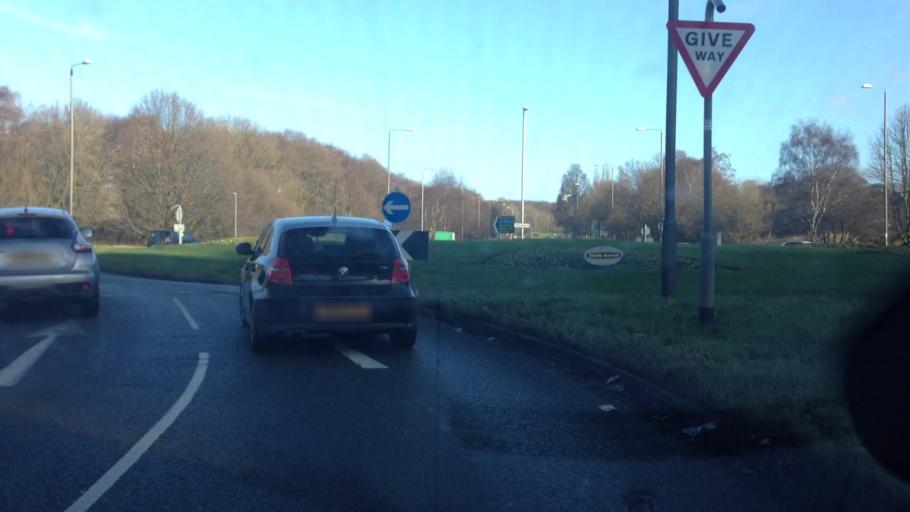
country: GB
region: England
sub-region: City and Borough of Leeds
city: Chapel Allerton
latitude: 53.8452
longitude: -1.5491
